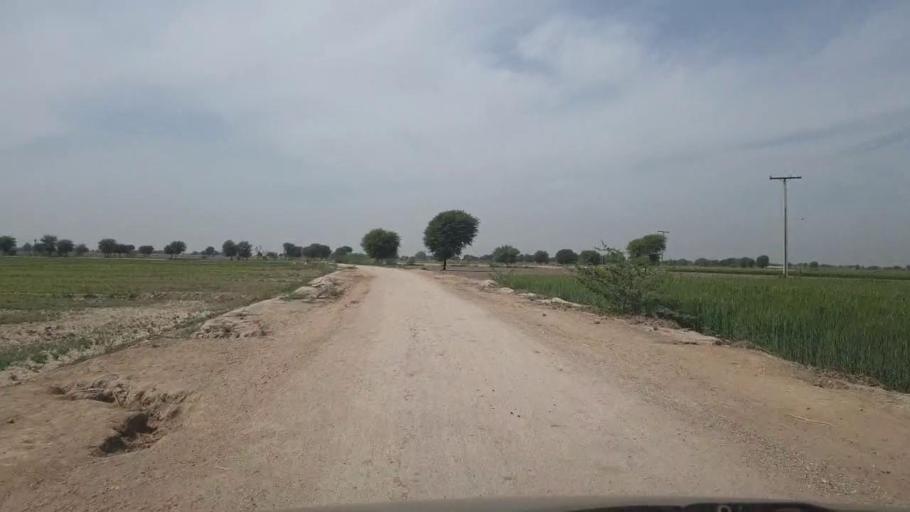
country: PK
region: Sindh
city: Kunri
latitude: 25.2387
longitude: 69.6666
